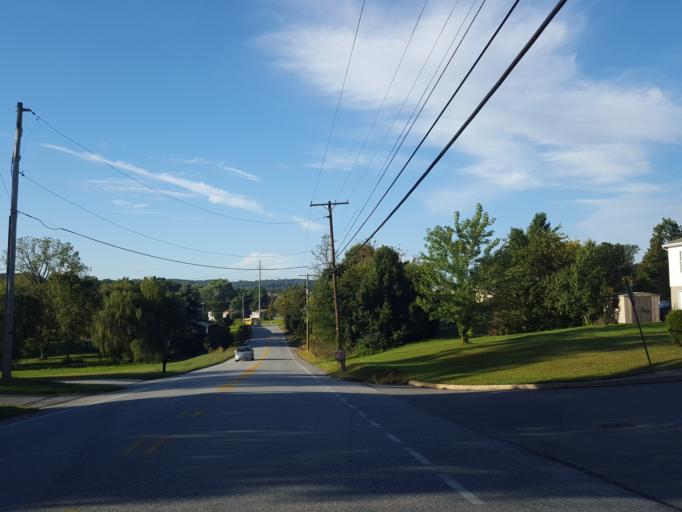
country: US
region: Pennsylvania
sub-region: York County
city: Windsor
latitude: 39.9379
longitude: -76.6033
